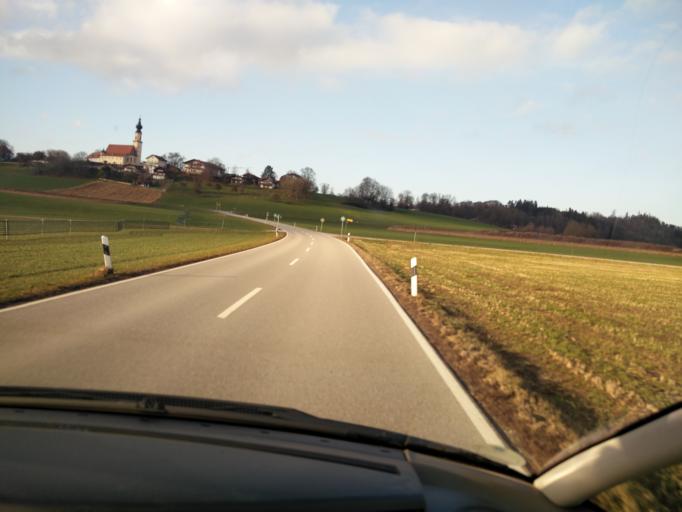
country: DE
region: Bavaria
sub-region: Upper Bavaria
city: Hoslwang
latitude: 47.9505
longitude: 12.3347
